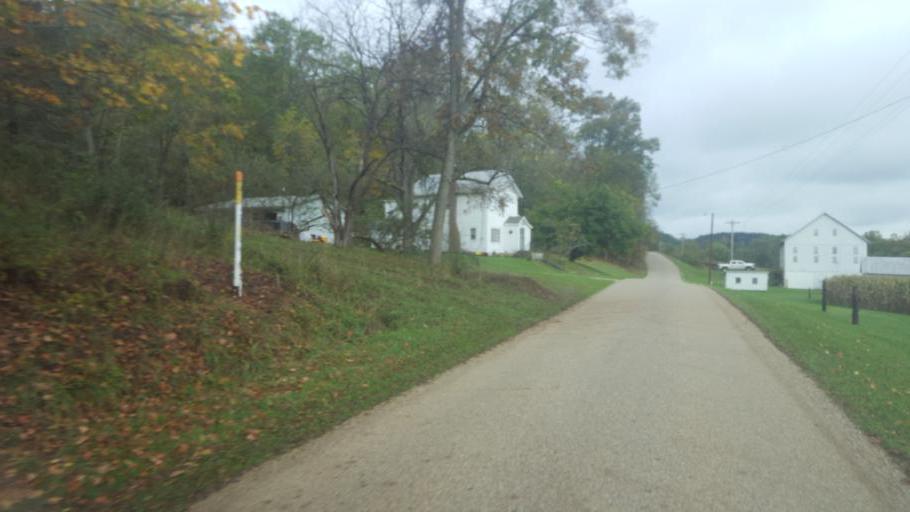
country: US
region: Ohio
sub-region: Ashland County
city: Loudonville
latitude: 40.6021
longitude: -82.2501
